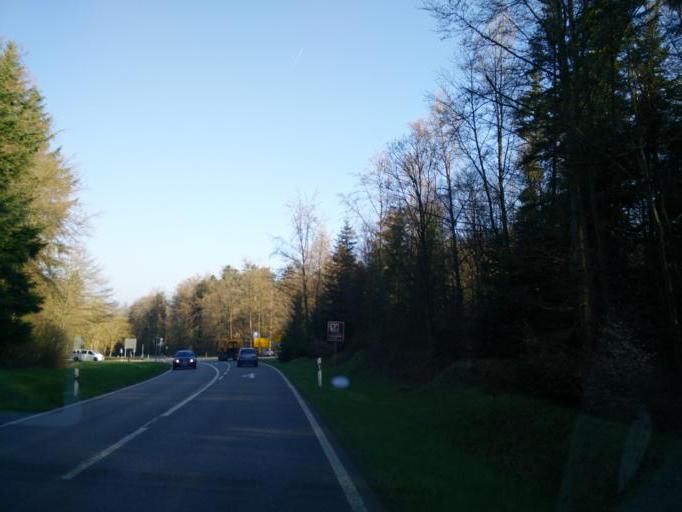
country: DE
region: Baden-Wuerttemberg
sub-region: Karlsruhe Region
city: Althengstett
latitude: 48.6799
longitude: 8.7755
